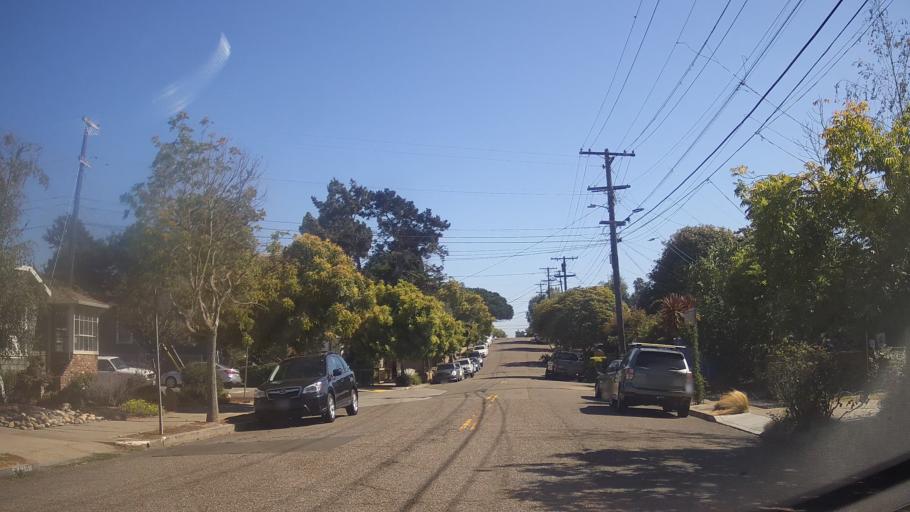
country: US
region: California
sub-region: Alameda County
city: Albany
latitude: 37.8754
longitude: -122.2887
